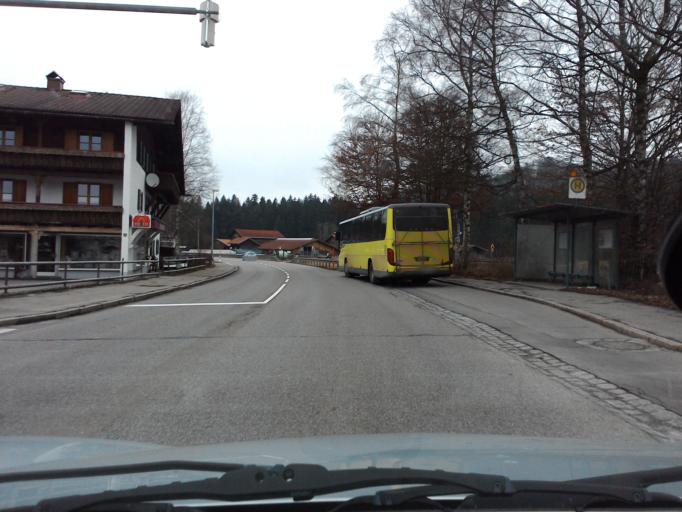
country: DE
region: Bavaria
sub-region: Swabia
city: Oberstdorf
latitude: 47.4372
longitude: 10.2755
